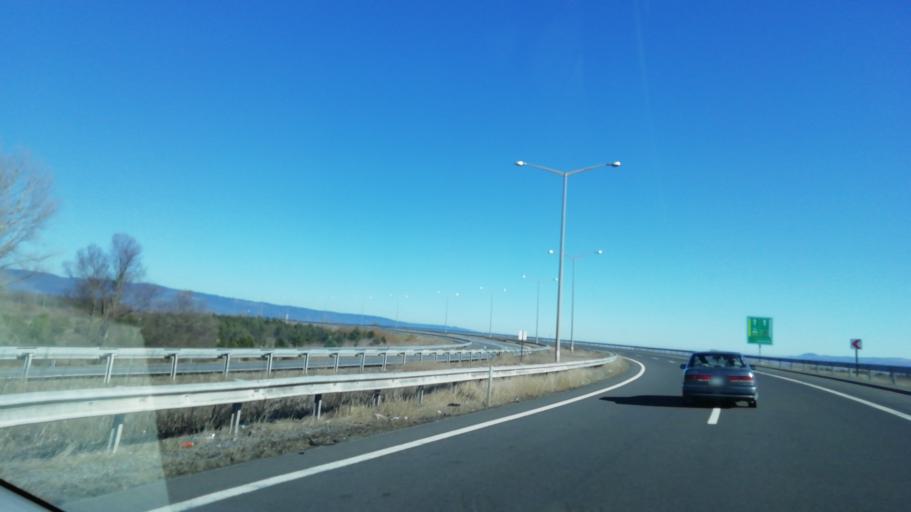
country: TR
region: Bolu
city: Gerede
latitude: 40.7328
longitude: 32.1903
